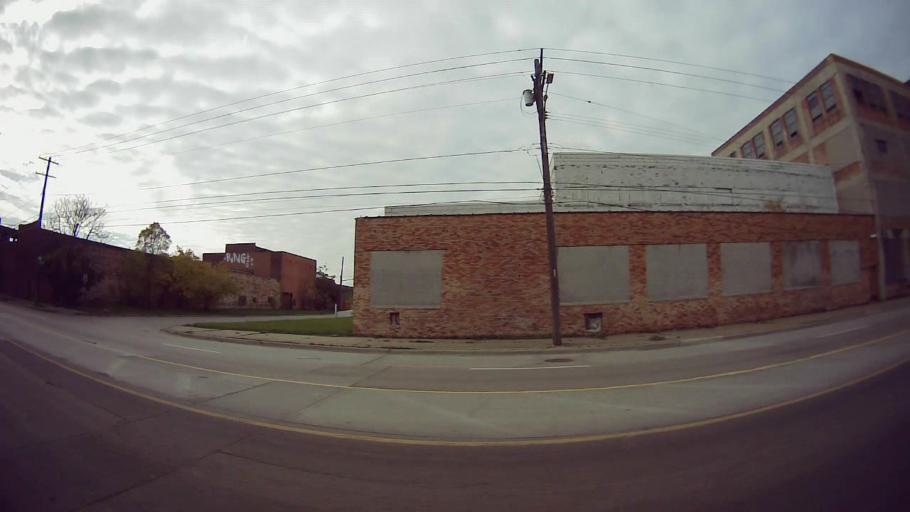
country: US
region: Michigan
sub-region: Wayne County
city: Hamtramck
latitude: 42.3688
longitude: -83.0552
